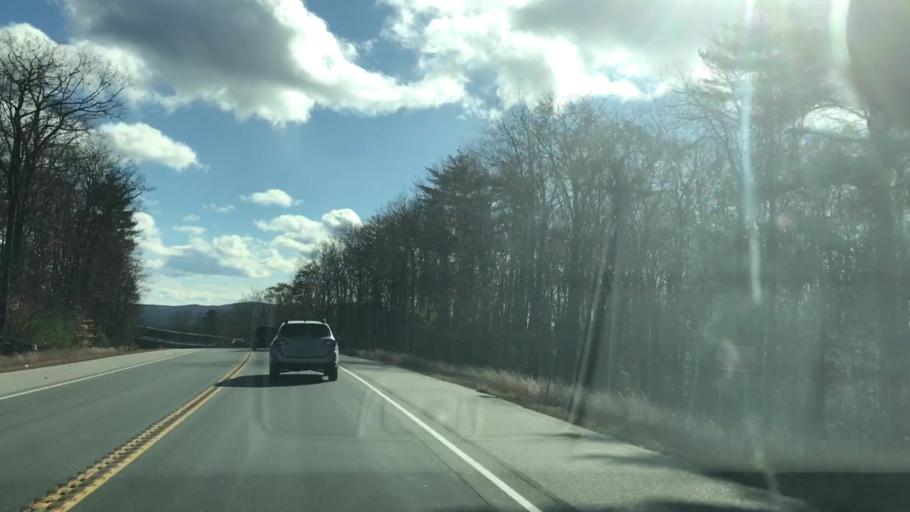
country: US
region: New Hampshire
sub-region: Strafford County
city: New Durham
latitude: 43.4637
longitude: -71.2232
